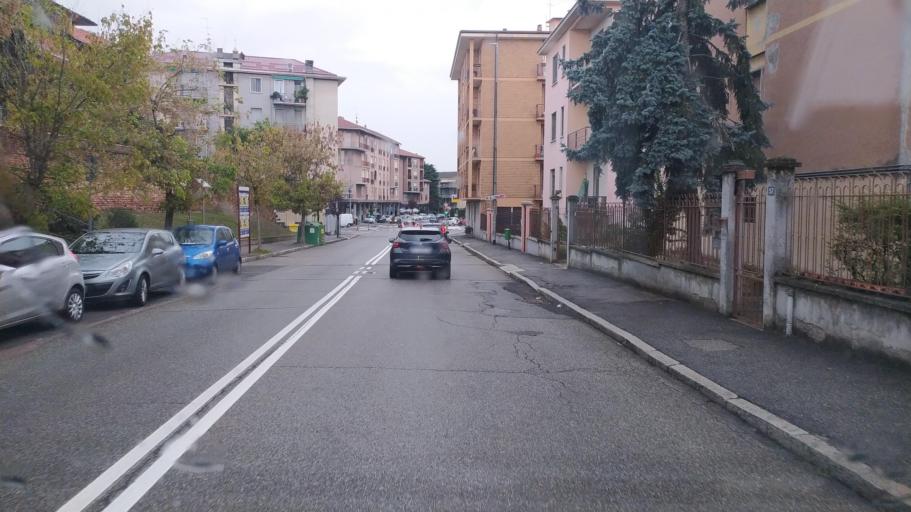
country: IT
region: Lombardy
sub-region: Provincia di Pavia
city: Pavia
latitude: 45.1942
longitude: 9.1655
